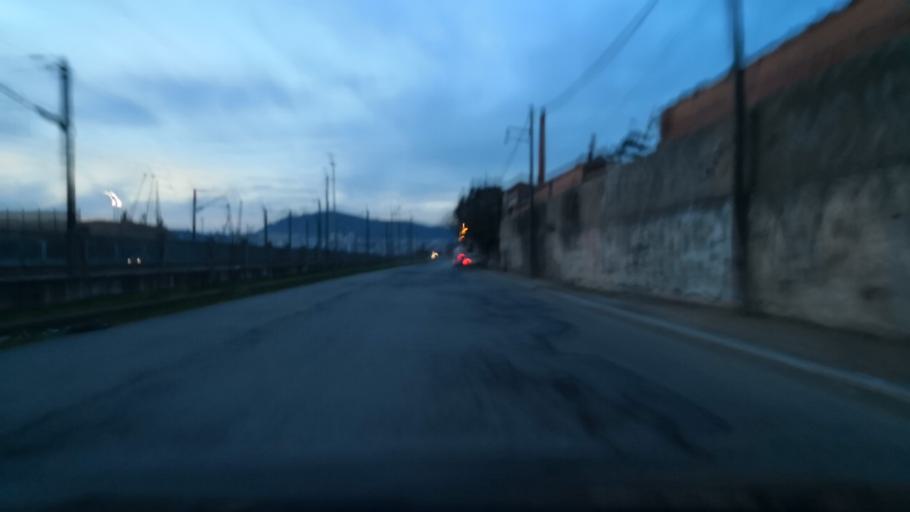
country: PT
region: Setubal
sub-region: Setubal
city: Setubal
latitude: 38.5179
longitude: -8.8729
